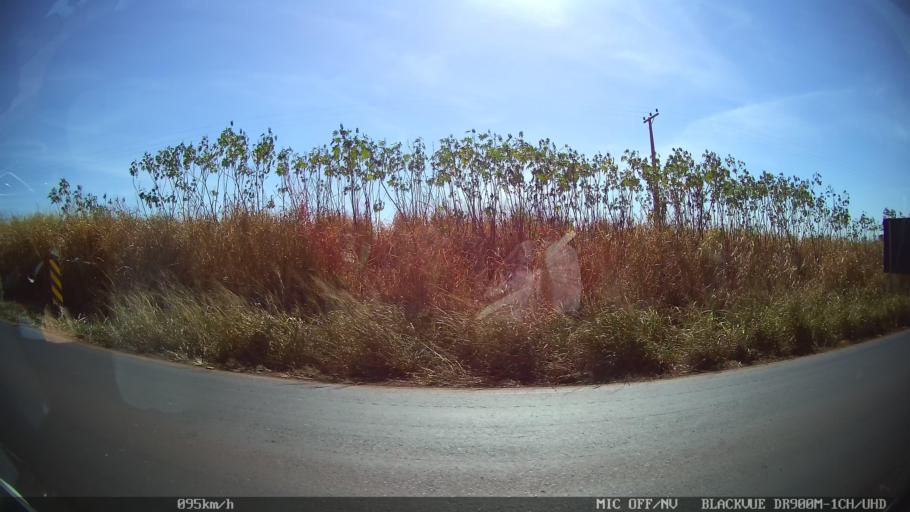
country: BR
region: Sao Paulo
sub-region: Barretos
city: Barretos
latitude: -20.4840
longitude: -48.5099
